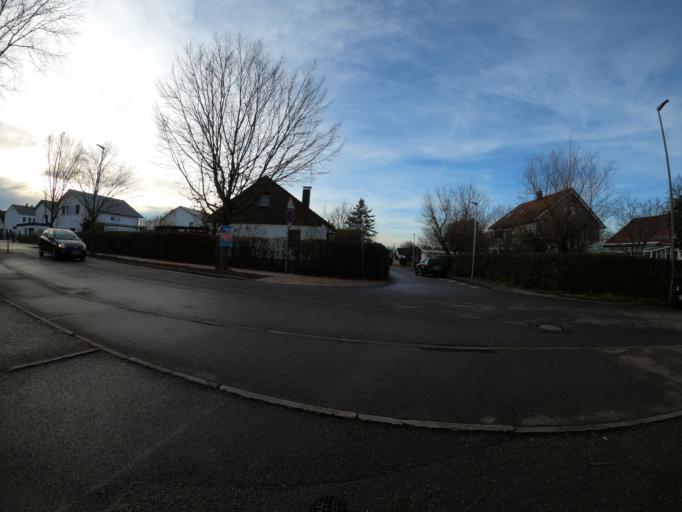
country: DE
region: Baden-Wuerttemberg
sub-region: Regierungsbezirk Stuttgart
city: Heiningen
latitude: 48.6584
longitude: 9.6433
